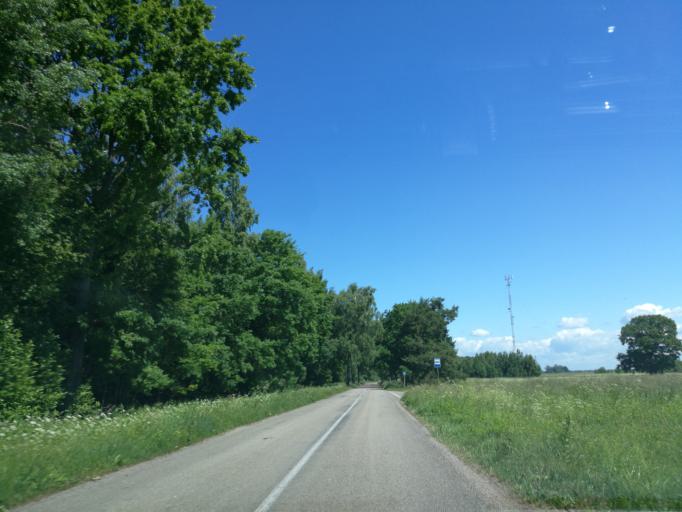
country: LT
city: Neringa
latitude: 55.3818
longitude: 21.2295
